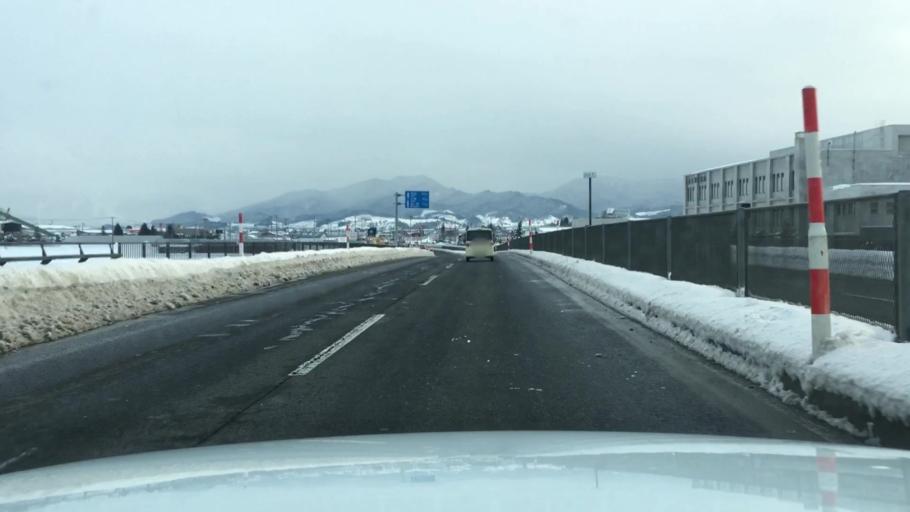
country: JP
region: Aomori
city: Hirosaki
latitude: 40.5889
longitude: 140.5067
